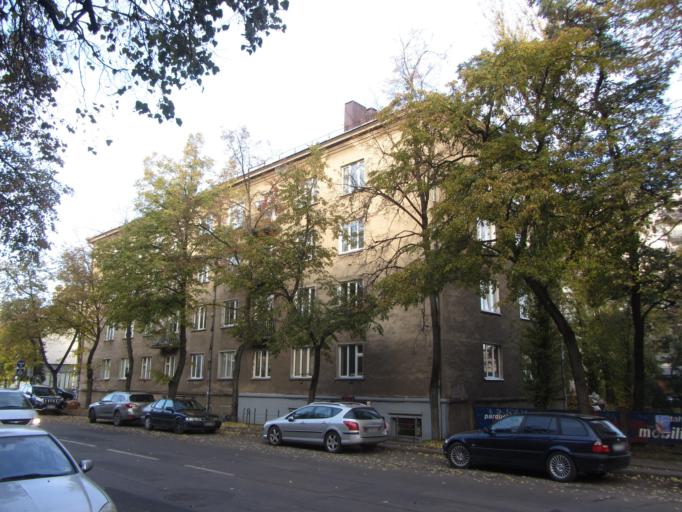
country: LT
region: Vilnius County
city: Naujamiestis
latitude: 54.6781
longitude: 25.2637
